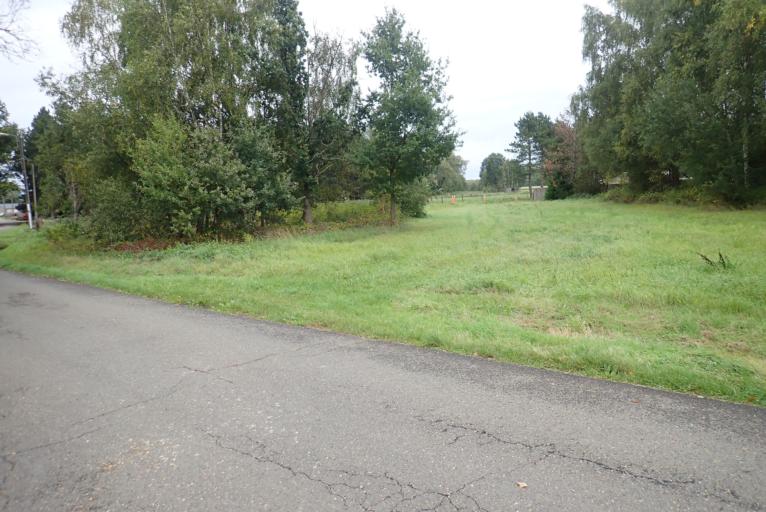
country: BE
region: Flanders
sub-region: Provincie Antwerpen
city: Heist-op-den-Berg
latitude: 51.0639
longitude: 4.7515
